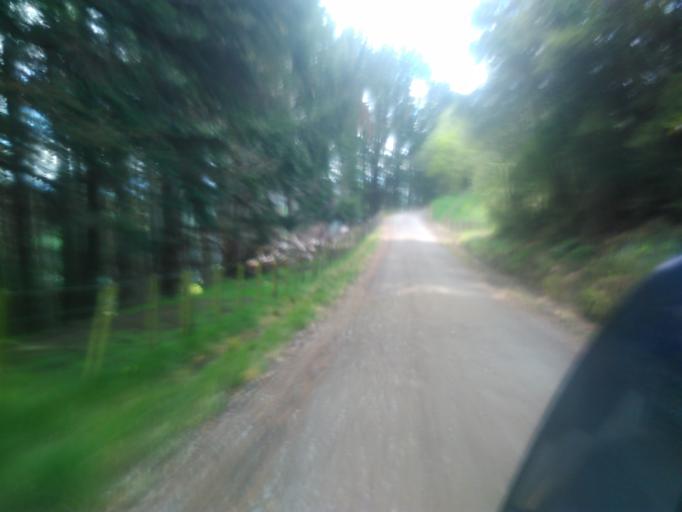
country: NZ
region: Hawke's Bay
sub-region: Wairoa District
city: Wairoa
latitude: -38.7733
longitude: 177.6376
